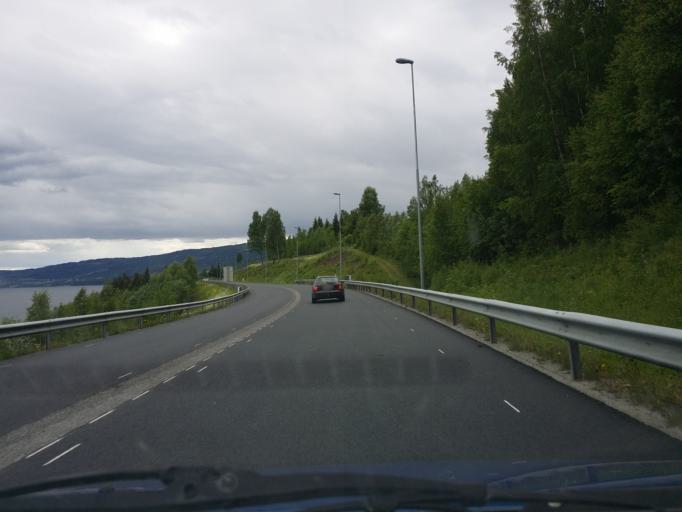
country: NO
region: Oppland
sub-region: Lillehammer
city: Lillehammer
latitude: 61.0590
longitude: 10.4313
